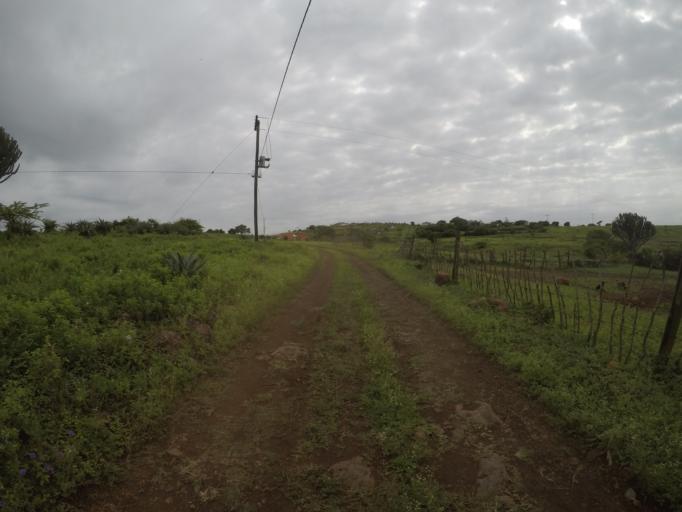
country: ZA
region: KwaZulu-Natal
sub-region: uThungulu District Municipality
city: Empangeni
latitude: -28.6395
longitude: 31.9038
